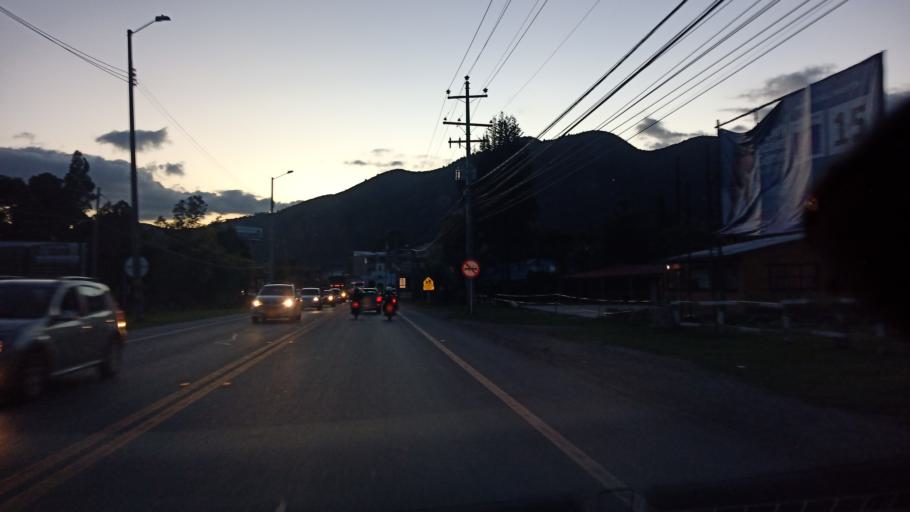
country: CO
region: Cundinamarca
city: Chia
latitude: 4.8492
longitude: -74.0761
